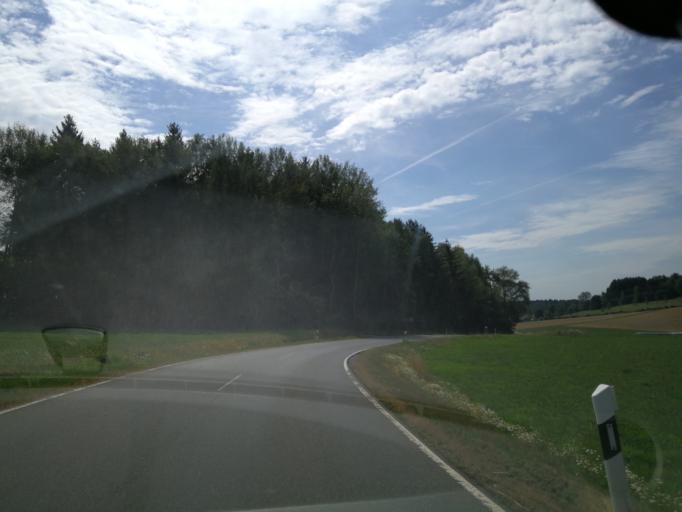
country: DE
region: Bavaria
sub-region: Upper Palatinate
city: Falkenstein
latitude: 49.0882
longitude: 12.5035
